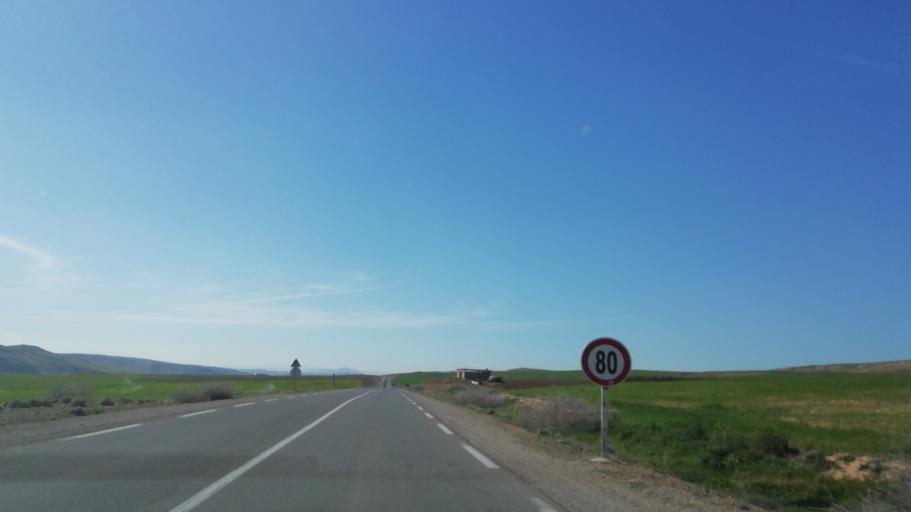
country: DZ
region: Mascara
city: Oued el Abtal
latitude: 35.4447
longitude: 0.8262
